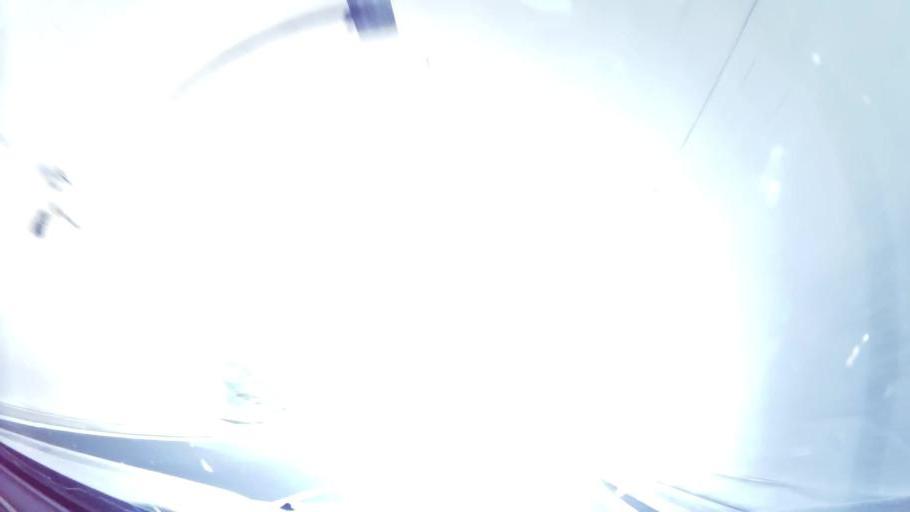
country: GR
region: Central Macedonia
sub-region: Nomos Imathias
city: Veroia
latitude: 40.4395
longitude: 22.1814
